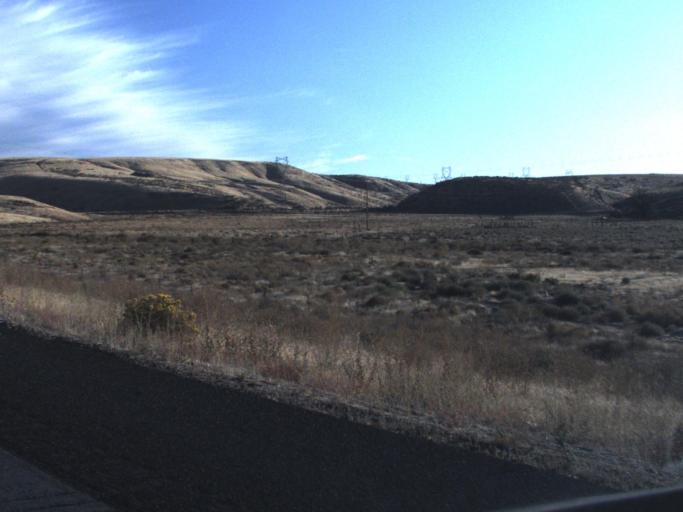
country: US
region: Washington
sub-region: Franklin County
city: Basin City
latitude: 46.5416
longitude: -119.0098
